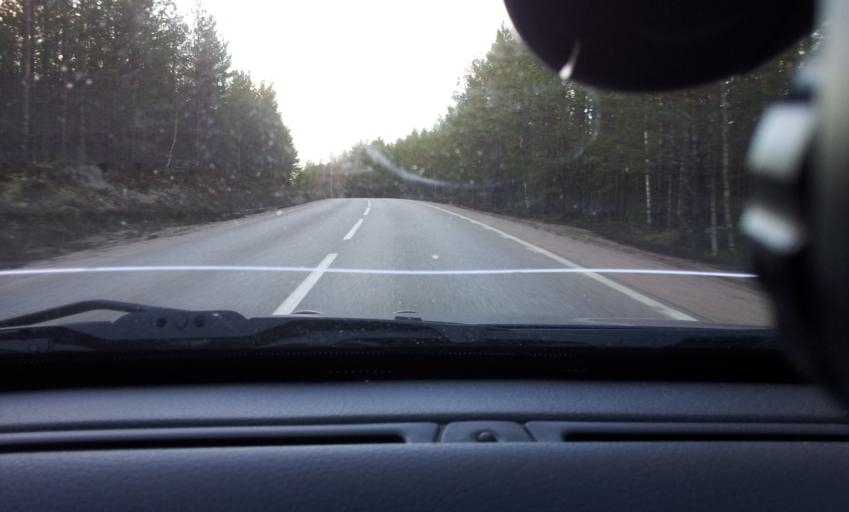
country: SE
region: Vaesternorrland
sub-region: Ange Kommun
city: Ange
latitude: 62.0902
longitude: 15.0920
